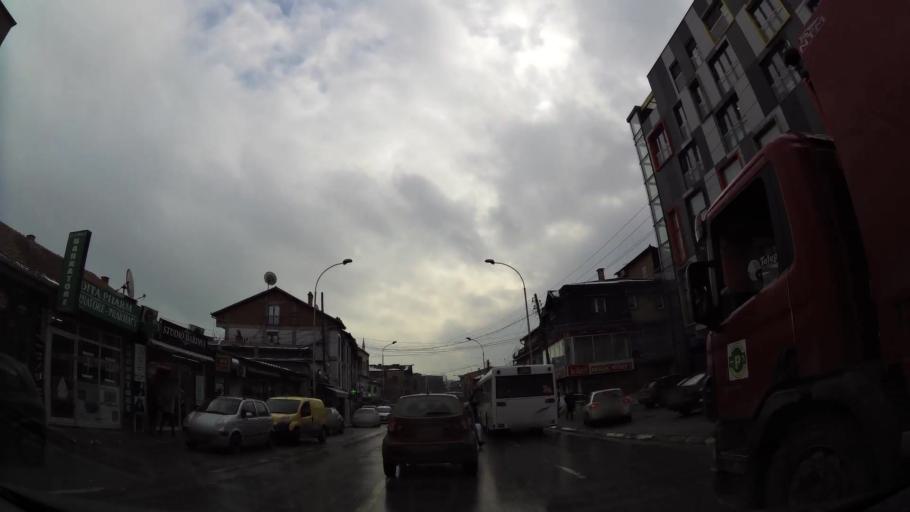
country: XK
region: Pristina
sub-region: Komuna e Prishtines
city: Pristina
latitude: 42.6707
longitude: 21.1623
